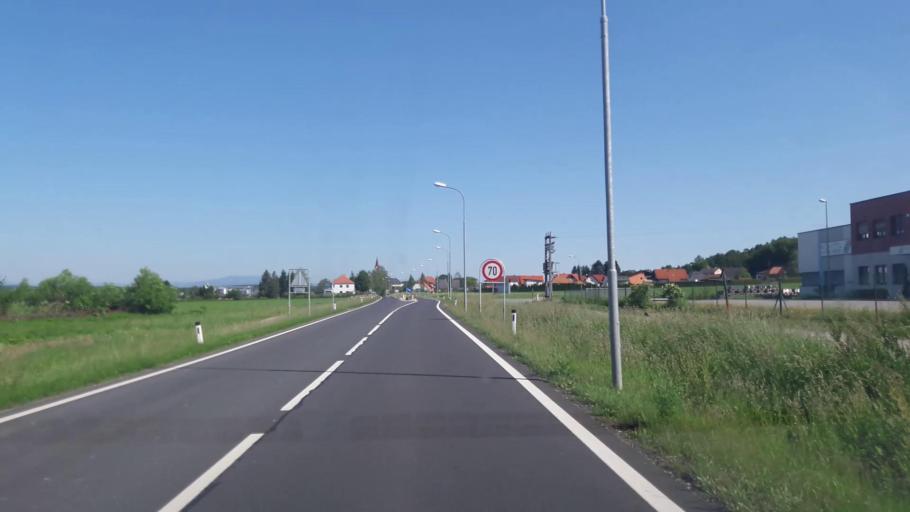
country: AT
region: Burgenland
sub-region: Politischer Bezirk Jennersdorf
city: Deutsch Kaltenbrunn
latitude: 47.0781
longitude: 16.1110
